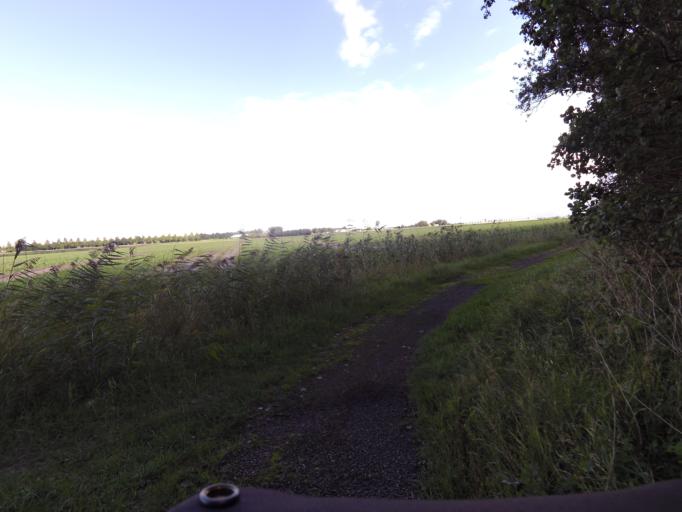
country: NL
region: North Brabant
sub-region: Gemeente Steenbergen
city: Nieuw-Vossemeer
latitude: 51.6825
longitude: 4.2208
